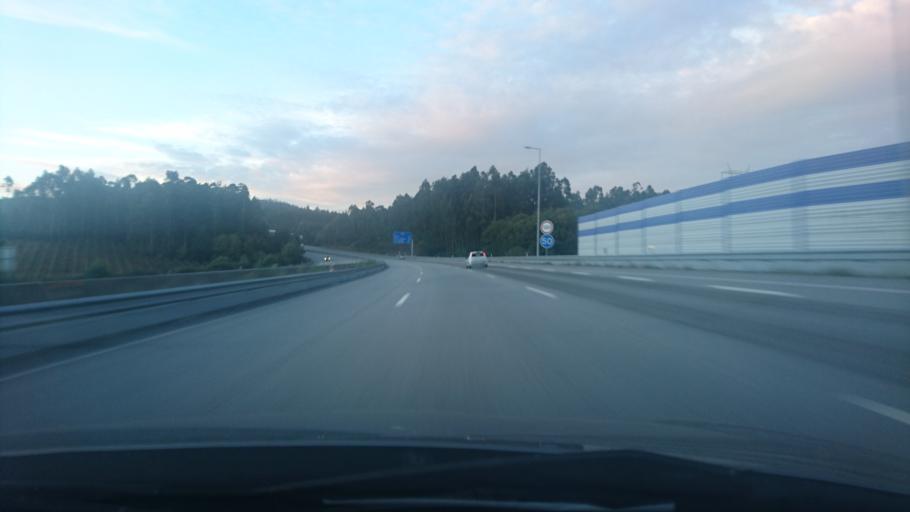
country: PT
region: Aveiro
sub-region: Santa Maria da Feira
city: Lobao
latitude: 40.9851
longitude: -8.4667
